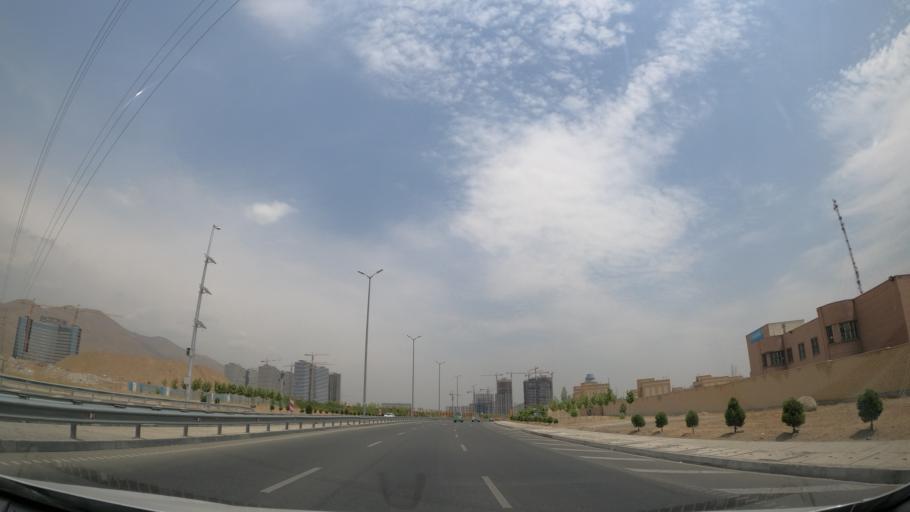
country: IR
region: Tehran
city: Shahr-e Qods
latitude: 35.7515
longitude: 51.1664
